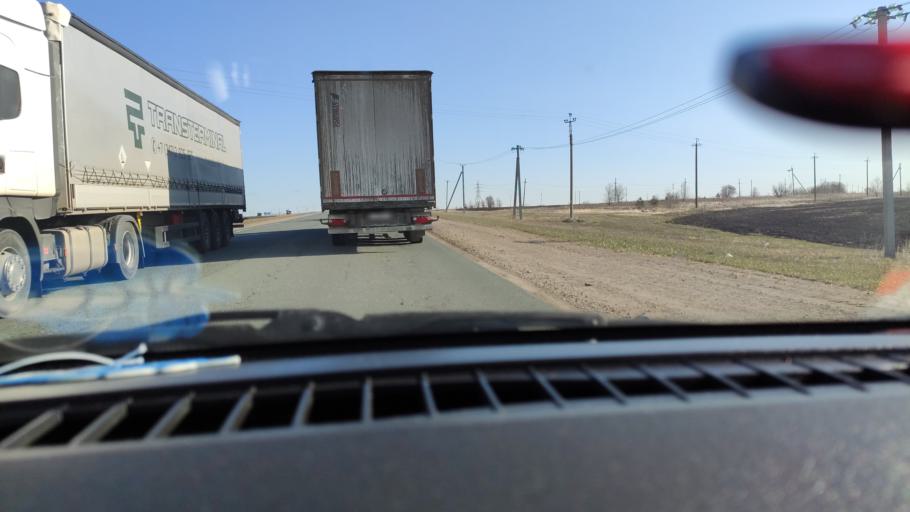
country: RU
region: Samara
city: Varlamovo
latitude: 53.1818
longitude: 48.2877
